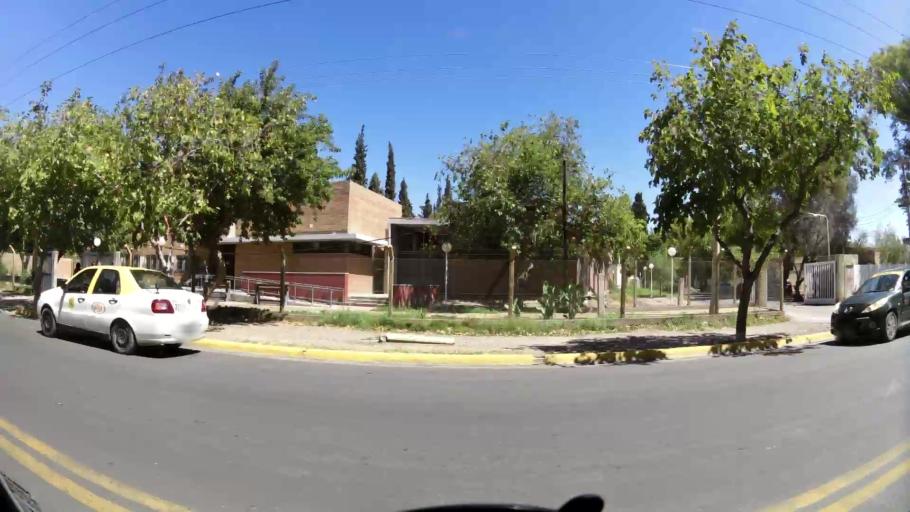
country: AR
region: San Juan
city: San Juan
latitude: -31.5273
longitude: -68.5548
